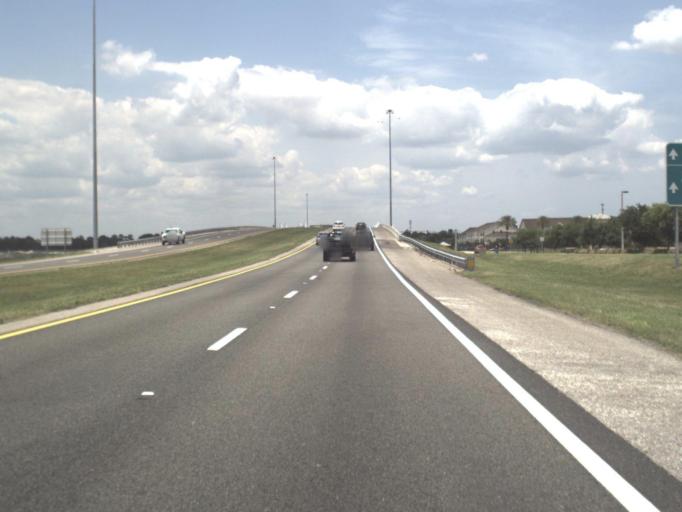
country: US
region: Florida
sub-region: Duval County
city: Jacksonville
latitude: 30.3351
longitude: -81.5521
